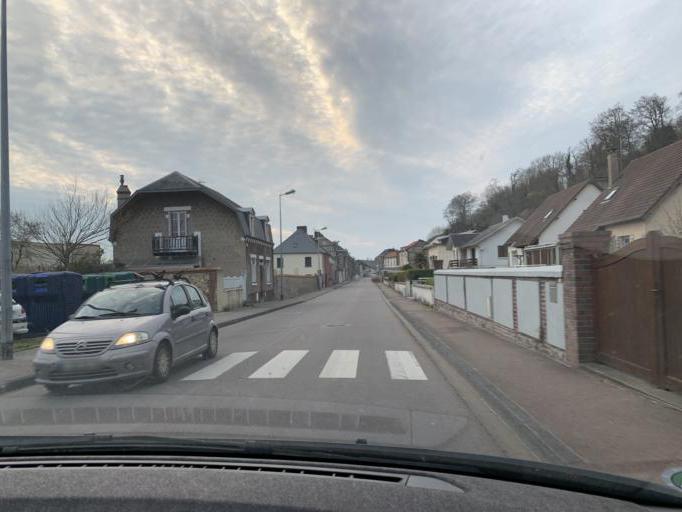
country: FR
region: Haute-Normandie
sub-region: Departement de la Seine-Maritime
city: Fecamp
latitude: 49.7582
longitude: 0.3910
